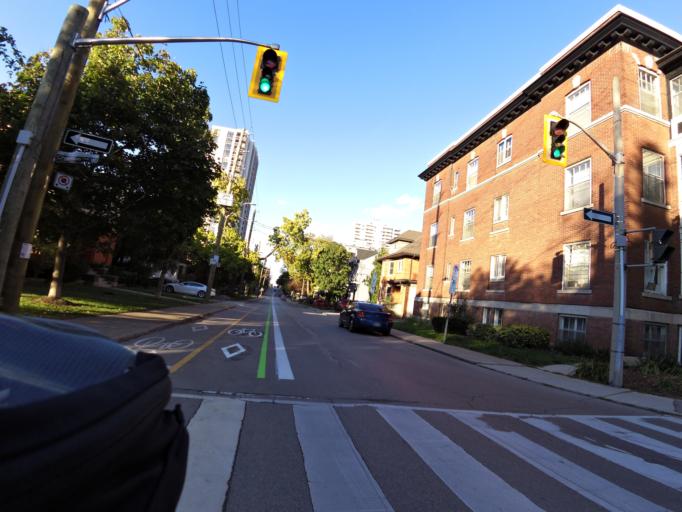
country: CA
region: Ontario
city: Hamilton
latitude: 43.2509
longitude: -79.8768
